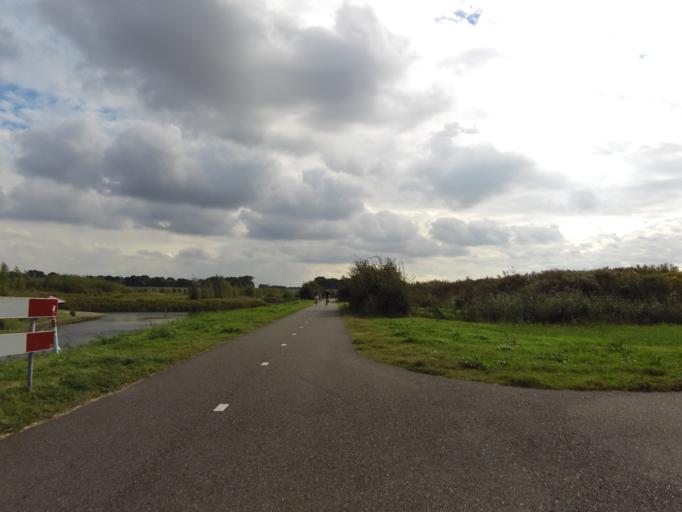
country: NL
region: South Holland
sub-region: Gemeente Rijnwoude
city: Benthuizen
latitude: 52.0648
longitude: 4.5508
